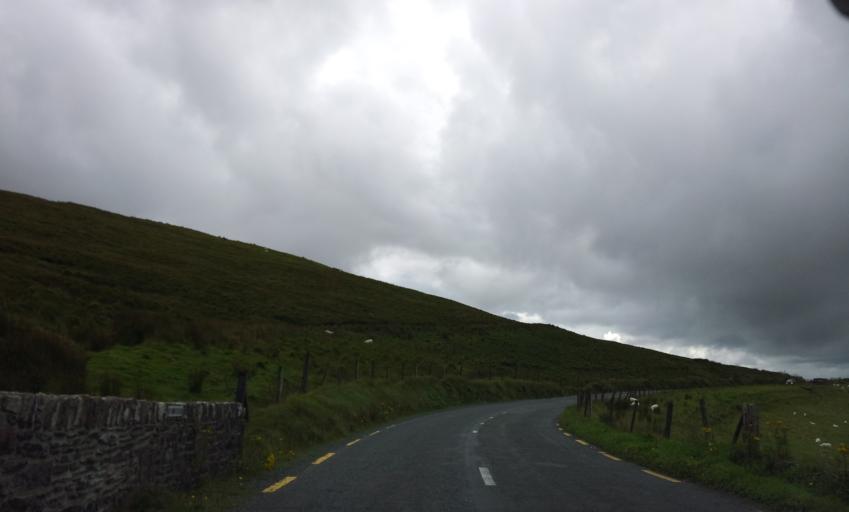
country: IE
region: Munster
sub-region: Ciarrai
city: Killorglin
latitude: 52.2006
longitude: -9.9286
